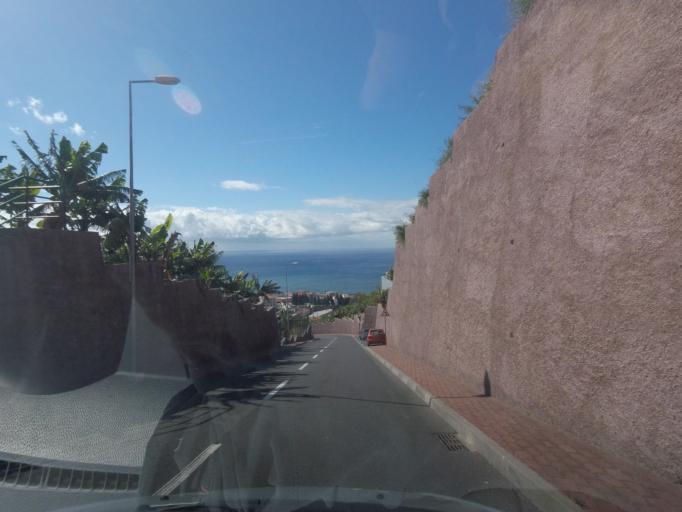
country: PT
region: Madeira
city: Camara de Lobos
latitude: 32.6509
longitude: -16.9724
